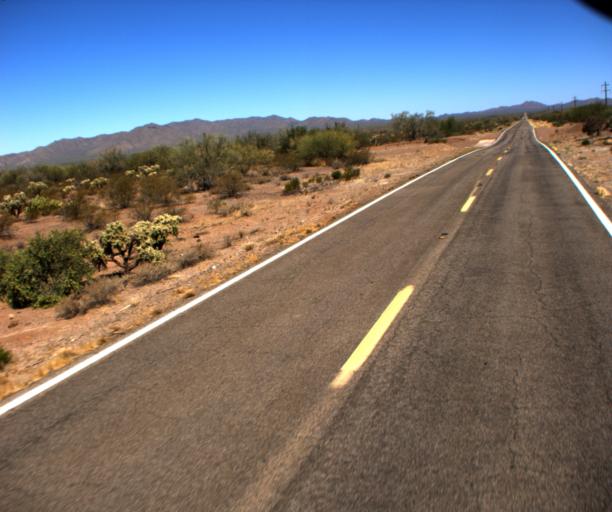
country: US
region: Arizona
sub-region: Pima County
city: Sells
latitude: 32.0750
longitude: -112.0453
